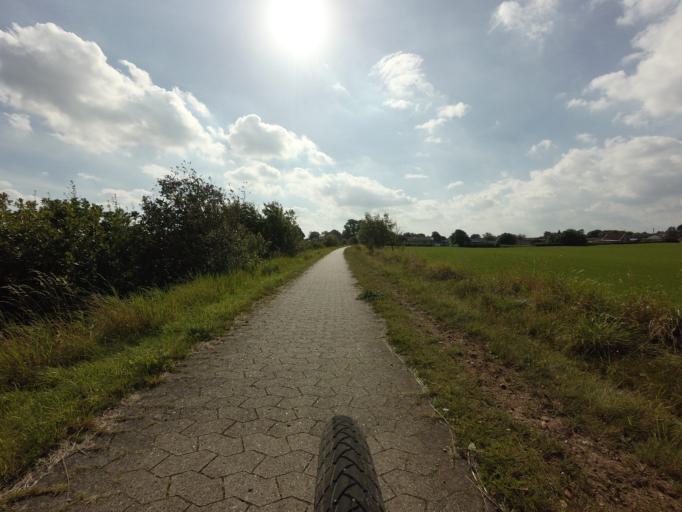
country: DK
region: Central Jutland
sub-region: Viborg Kommune
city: Viborg
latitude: 56.3659
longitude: 9.2997
